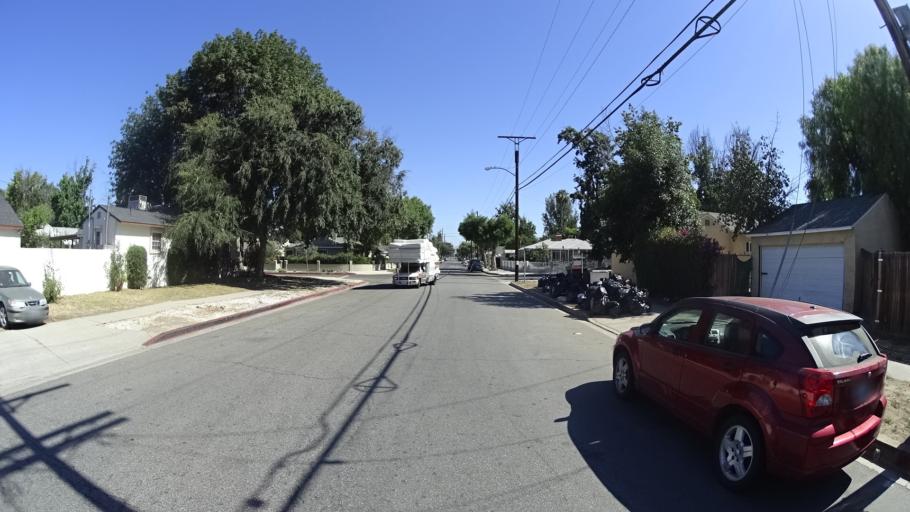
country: US
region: California
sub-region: Los Angeles County
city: Van Nuys
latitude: 34.1872
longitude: -118.4860
